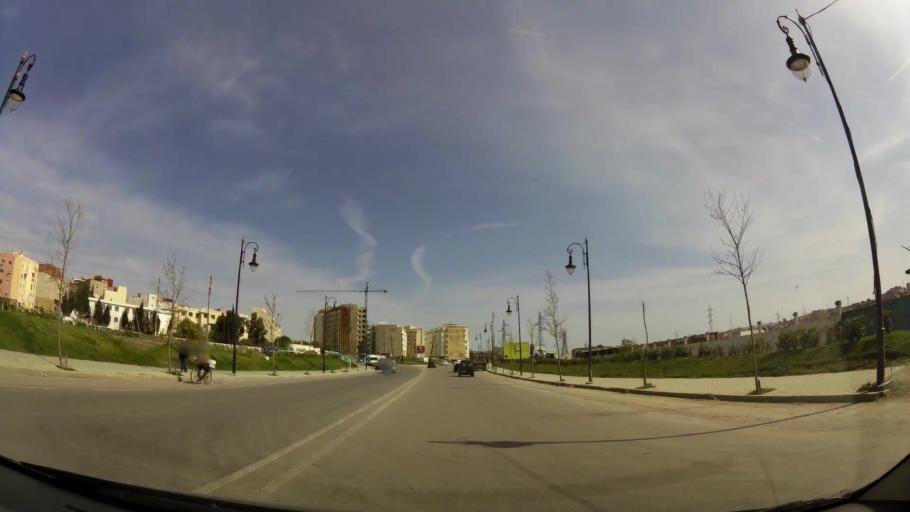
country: MA
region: Tanger-Tetouan
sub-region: Tanger-Assilah
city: Tangier
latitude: 35.7289
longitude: -5.8028
